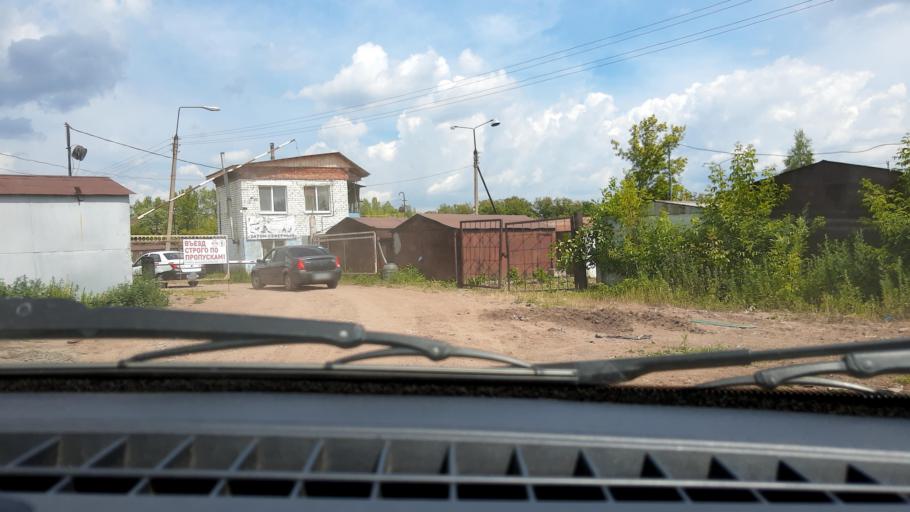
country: RU
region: Bashkortostan
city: Mikhaylovka
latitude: 54.7760
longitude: 55.9119
